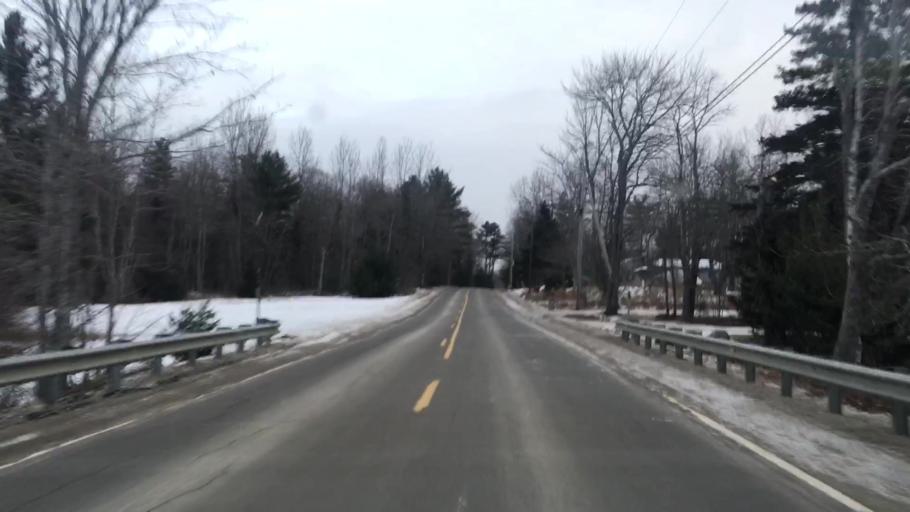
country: US
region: Maine
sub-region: Hancock County
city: Ellsworth
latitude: 44.6076
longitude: -68.3929
